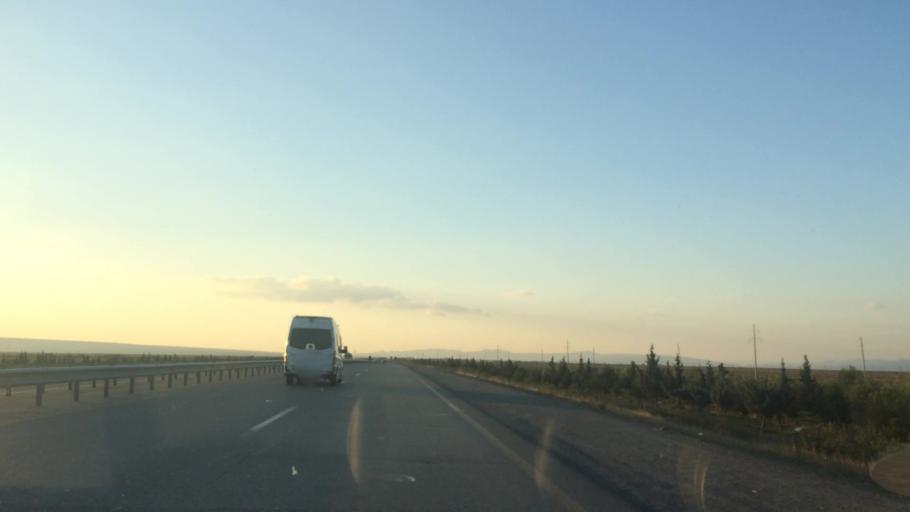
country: AZ
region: Baki
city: Qobustan
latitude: 39.9917
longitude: 49.1947
